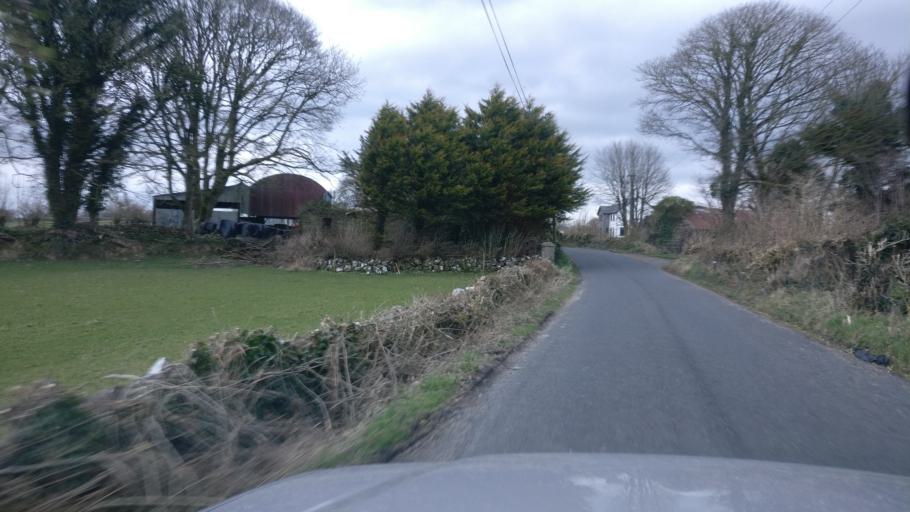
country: IE
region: Connaught
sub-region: County Galway
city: Loughrea
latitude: 53.2491
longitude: -8.5131
